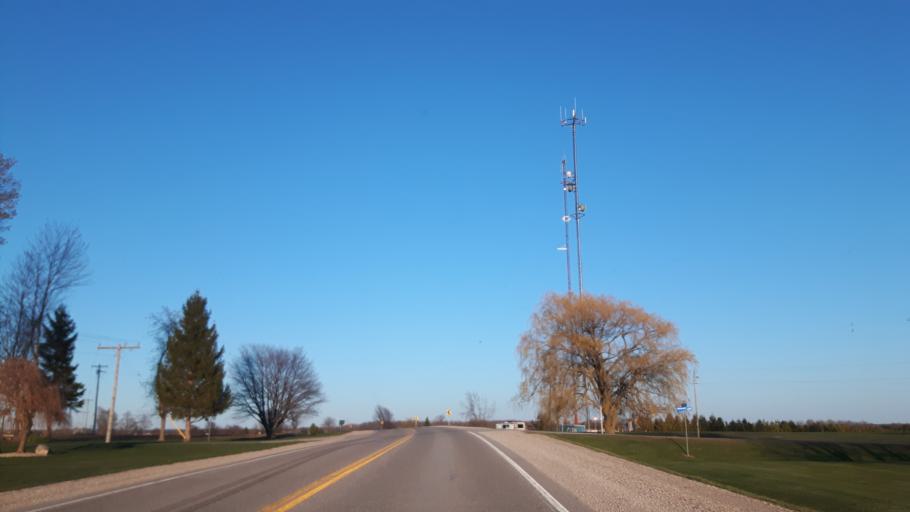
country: CA
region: Ontario
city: Bluewater
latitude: 43.5225
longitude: -81.5518
